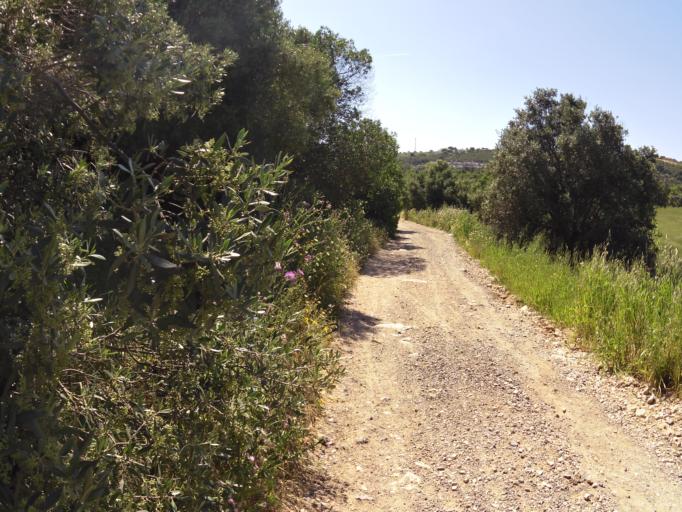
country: PT
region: Faro
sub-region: Lagos
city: Lagos
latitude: 37.1009
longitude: -8.7126
